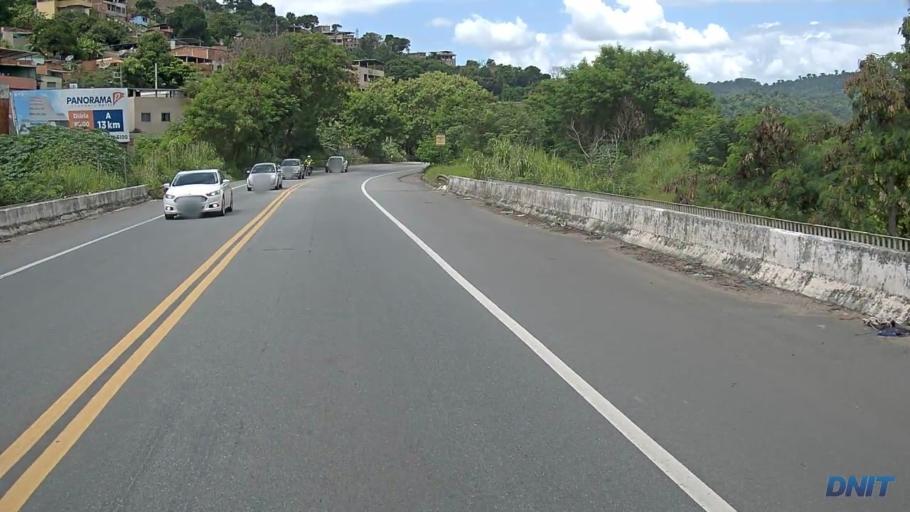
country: BR
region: Minas Gerais
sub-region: Coronel Fabriciano
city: Coronel Fabriciano
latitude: -19.5318
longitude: -42.6016
